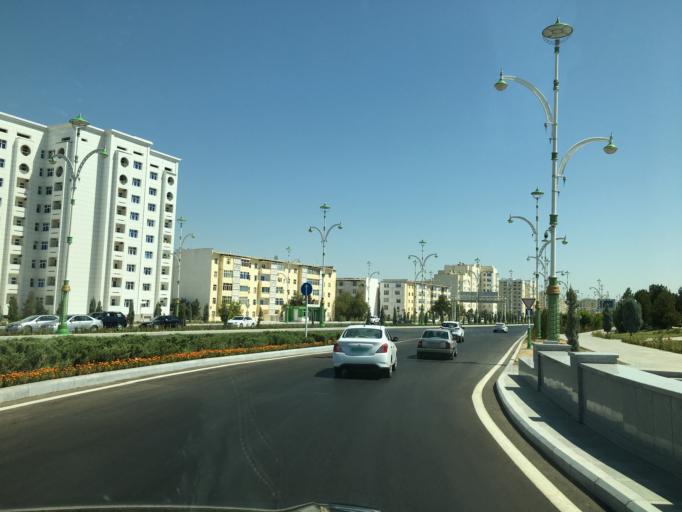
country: TM
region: Ahal
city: Ashgabat
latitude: 37.8952
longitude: 58.3793
